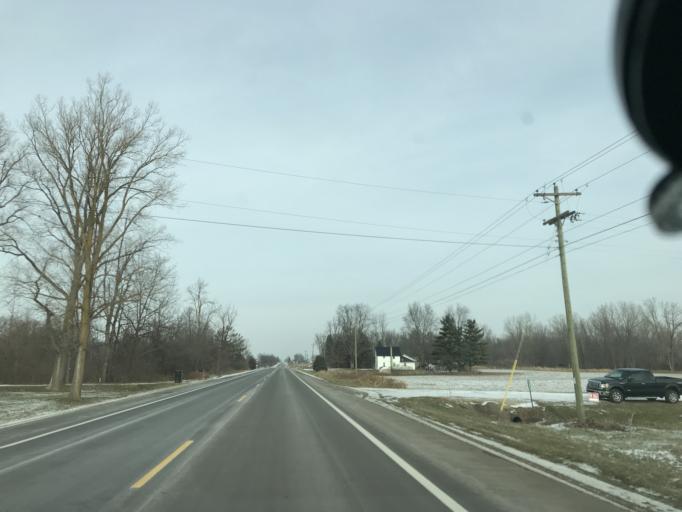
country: US
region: Michigan
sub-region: Ionia County
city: Lake Odessa
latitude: 42.8051
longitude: -85.0746
